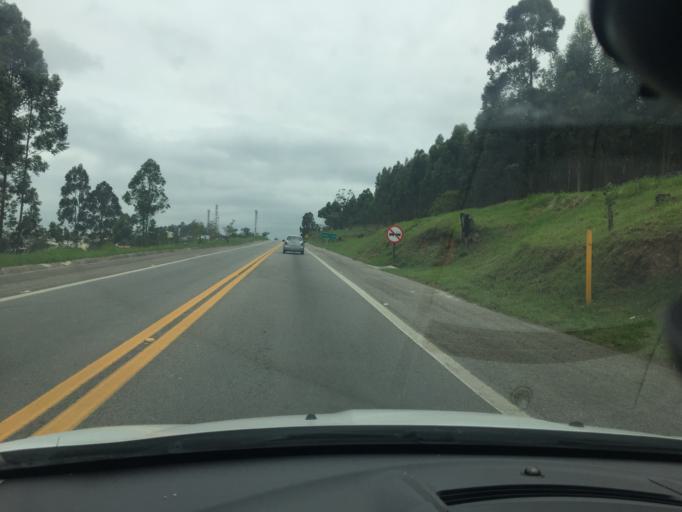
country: BR
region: Sao Paulo
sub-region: Jundiai
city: Jundiai
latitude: -23.1578
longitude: -46.8773
